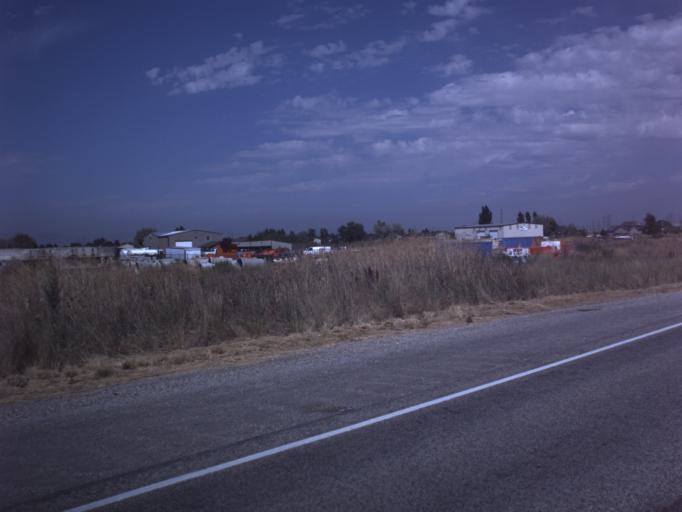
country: US
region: Utah
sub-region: Weber County
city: Farr West
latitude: 41.3259
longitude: -112.0322
